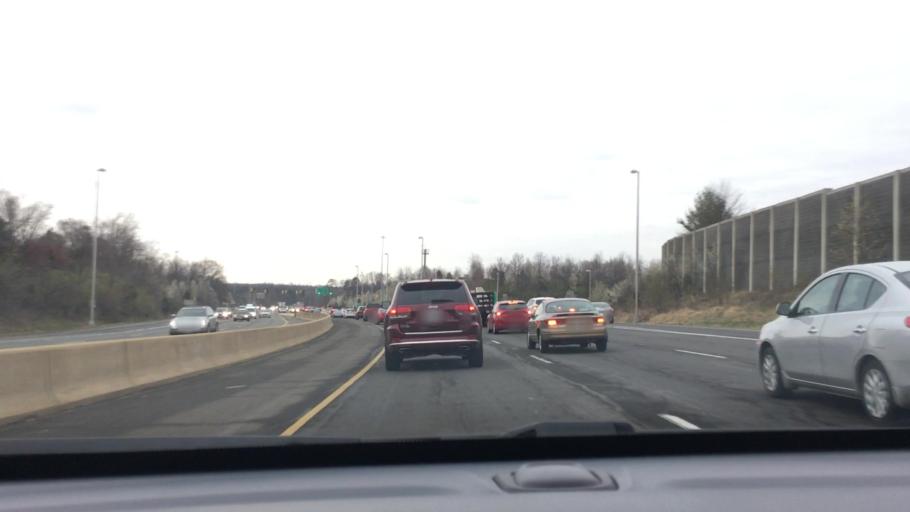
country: US
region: Virginia
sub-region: Fairfax County
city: Centreville
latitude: 38.8425
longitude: -77.4311
